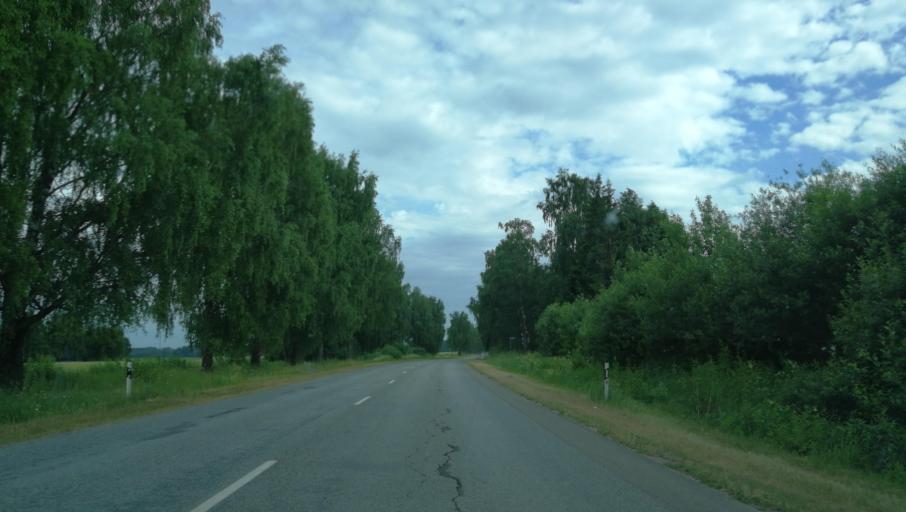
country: LV
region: Valmieras Rajons
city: Valmiera
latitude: 57.6375
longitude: 25.4453
